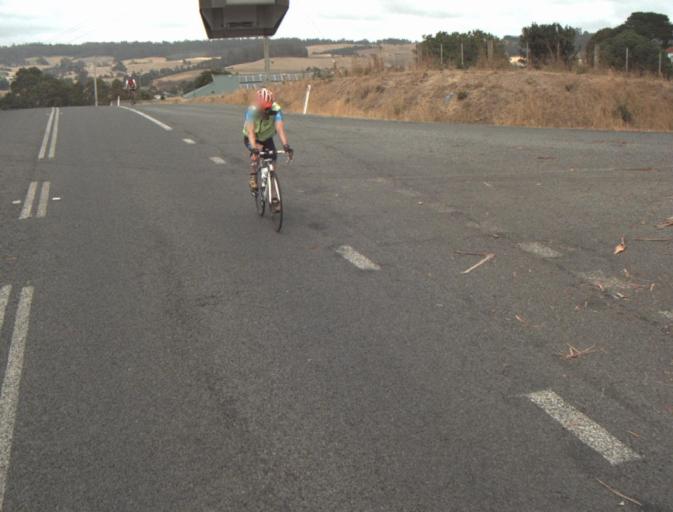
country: AU
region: Tasmania
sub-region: Dorset
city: Bridport
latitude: -41.1689
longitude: 147.2309
